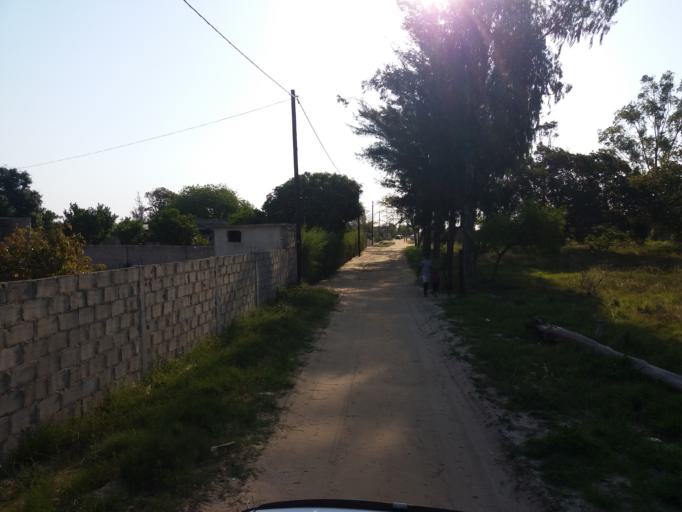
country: MZ
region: Maputo City
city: Maputo
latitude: -25.7626
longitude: 32.6085
